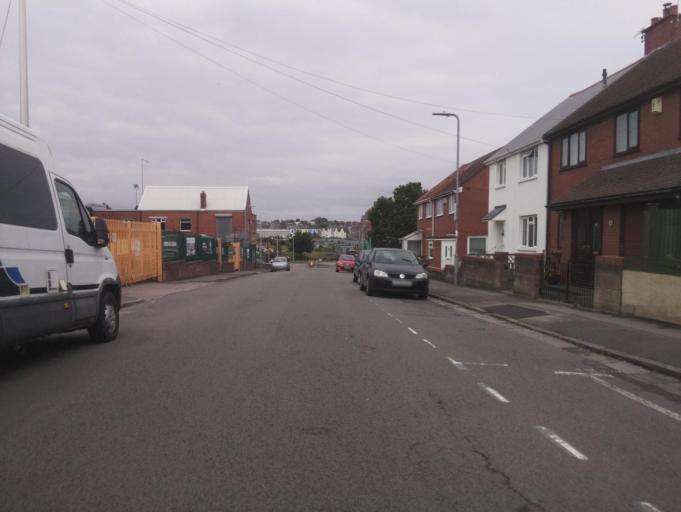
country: GB
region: Wales
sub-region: Vale of Glamorgan
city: Barry
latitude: 51.4092
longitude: -3.2620
